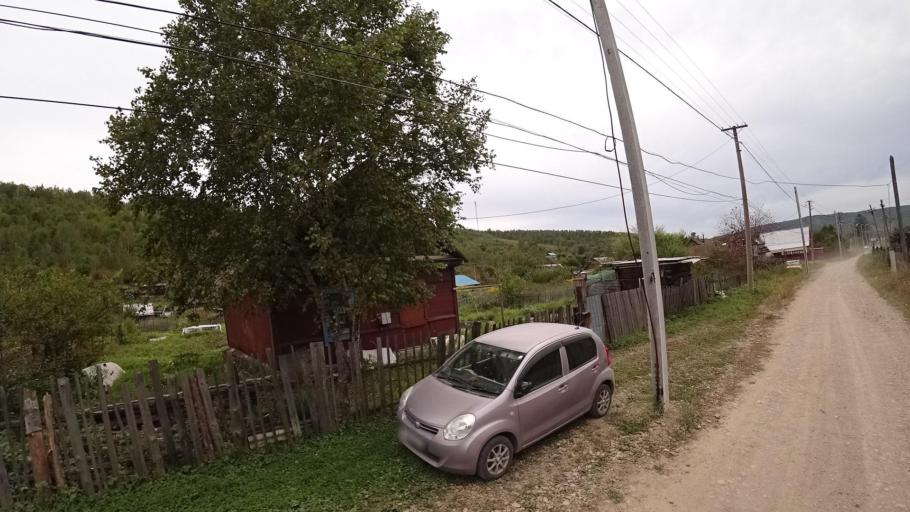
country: RU
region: Jewish Autonomous Oblast
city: Khingansk
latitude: 49.0238
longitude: 131.0706
